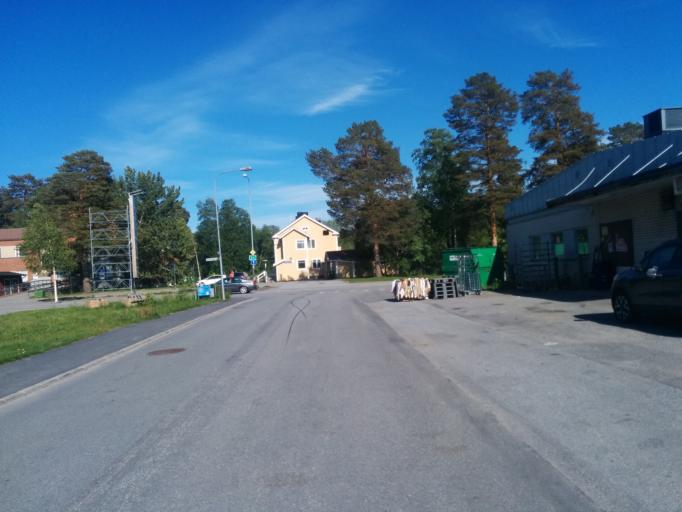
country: SE
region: Vaesterbotten
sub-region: Umea Kommun
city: Hoernefors
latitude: 63.6240
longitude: 19.9074
